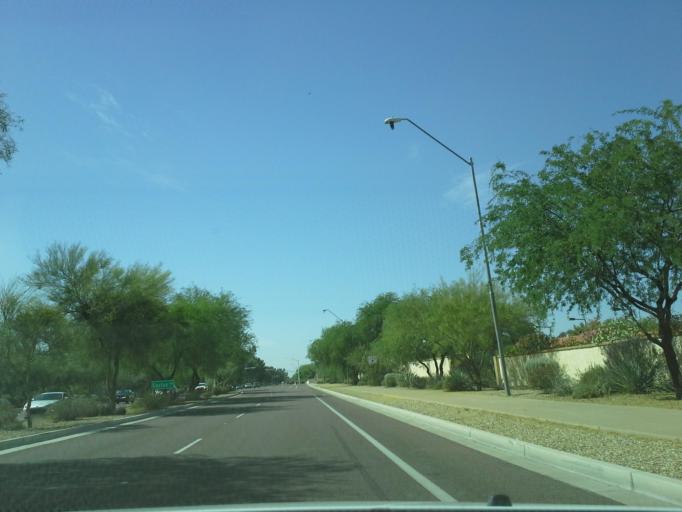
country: US
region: Arizona
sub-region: Maricopa County
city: Paradise Valley
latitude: 33.5989
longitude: -111.9087
